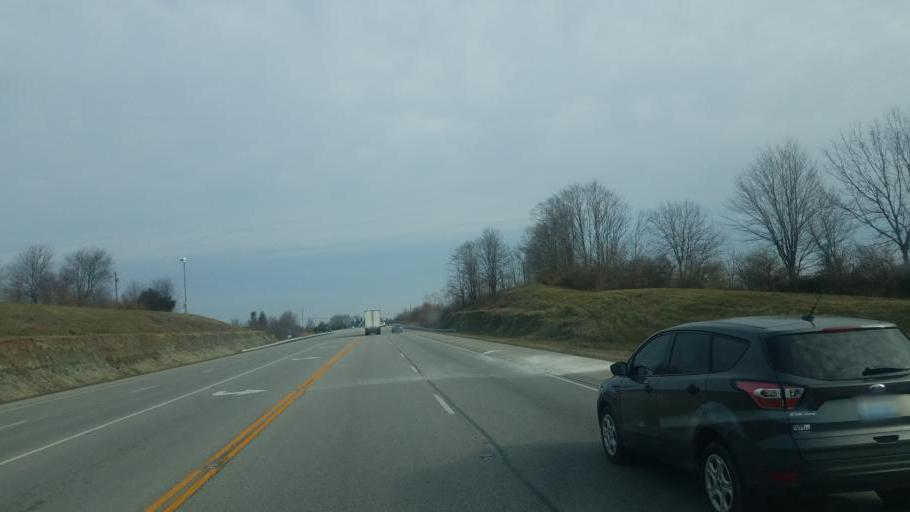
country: US
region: Kentucky
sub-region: Boyle County
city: Junction City
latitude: 37.5950
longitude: -84.7769
